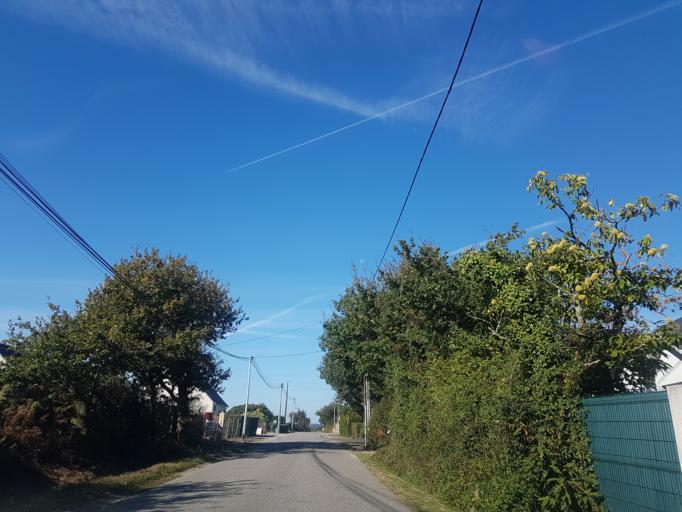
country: FR
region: Pays de la Loire
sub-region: Departement de la Loire-Atlantique
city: Petit-Mars
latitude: 47.3901
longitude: -1.4391
